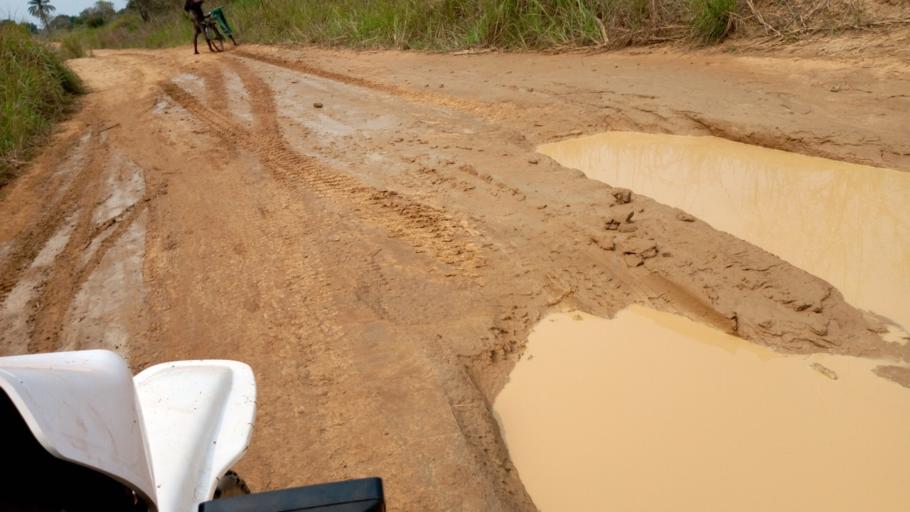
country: CD
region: Bandundu
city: Bandundu
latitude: -3.4826
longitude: 17.7857
